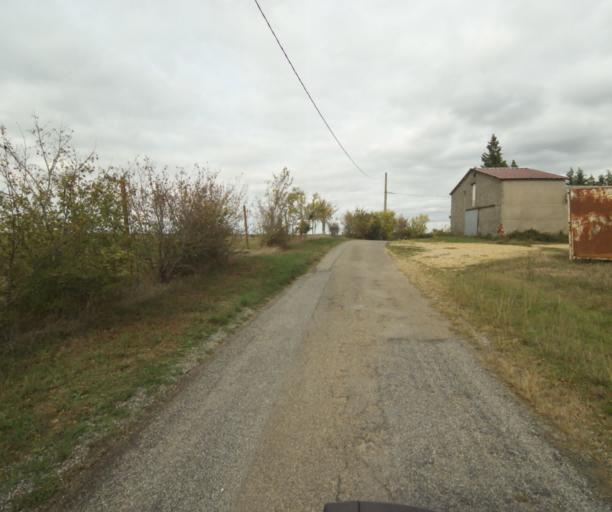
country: FR
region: Midi-Pyrenees
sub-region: Departement du Tarn-et-Garonne
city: Beaumont-de-Lomagne
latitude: 43.8306
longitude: 1.0752
